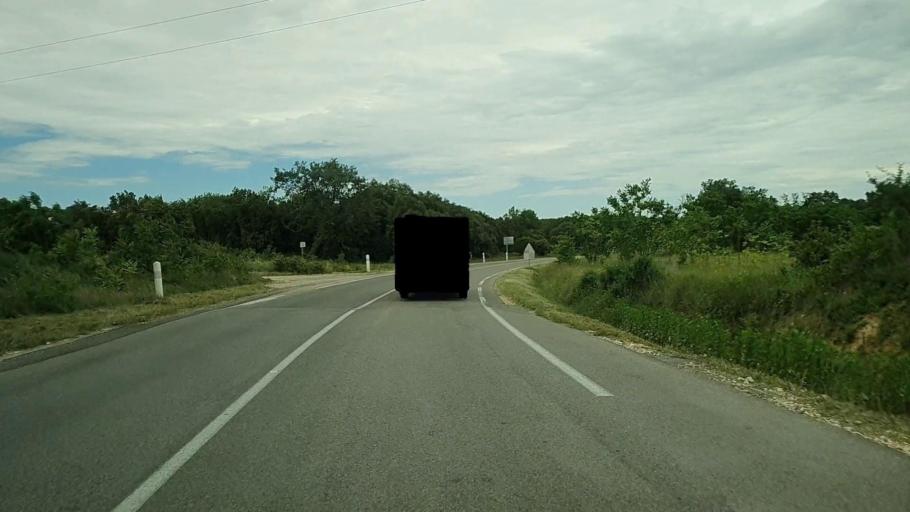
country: FR
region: Languedoc-Roussillon
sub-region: Departement du Gard
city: Connaux
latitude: 44.0583
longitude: 4.5700
